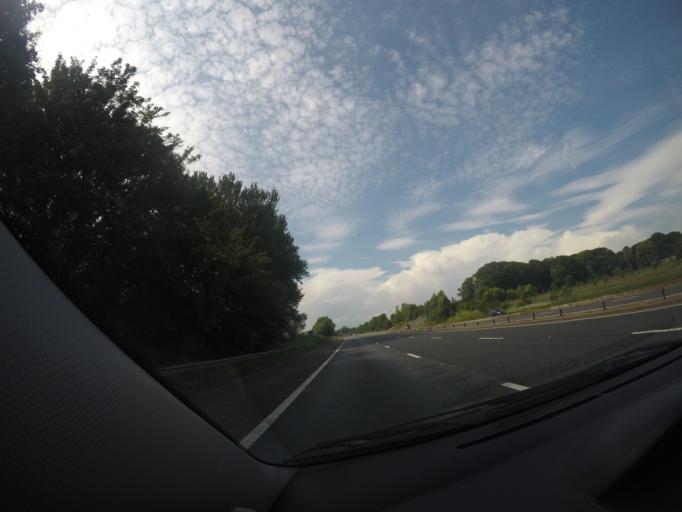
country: GB
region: England
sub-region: Cumbria
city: Carlisle
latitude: 54.9225
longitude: -2.9101
